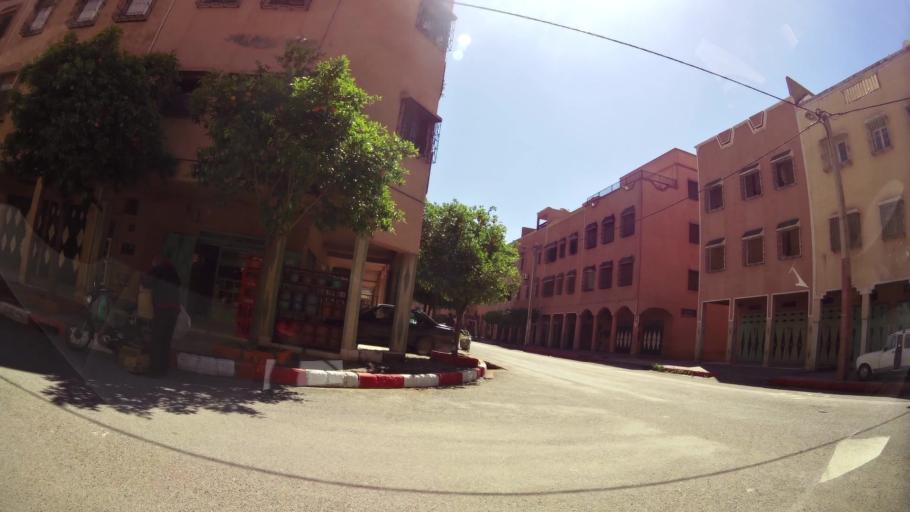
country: MA
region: Marrakech-Tensift-Al Haouz
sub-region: Marrakech
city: Marrakesh
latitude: 31.6317
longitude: -8.0695
